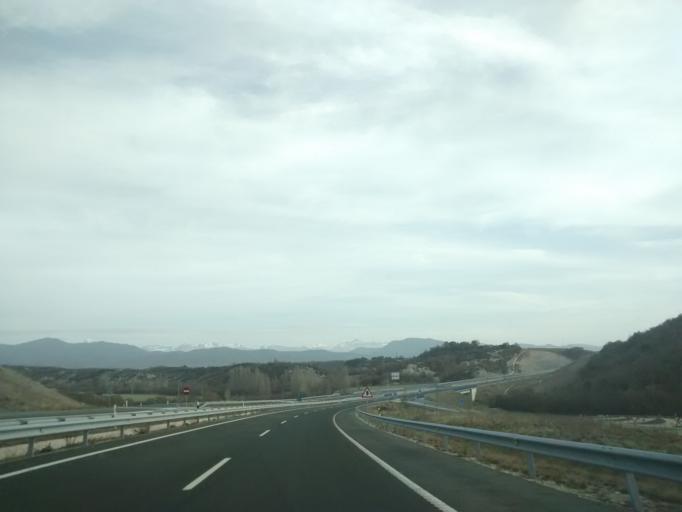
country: ES
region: Aragon
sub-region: Provincia de Zaragoza
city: Mianos
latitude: 42.6115
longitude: -0.9347
